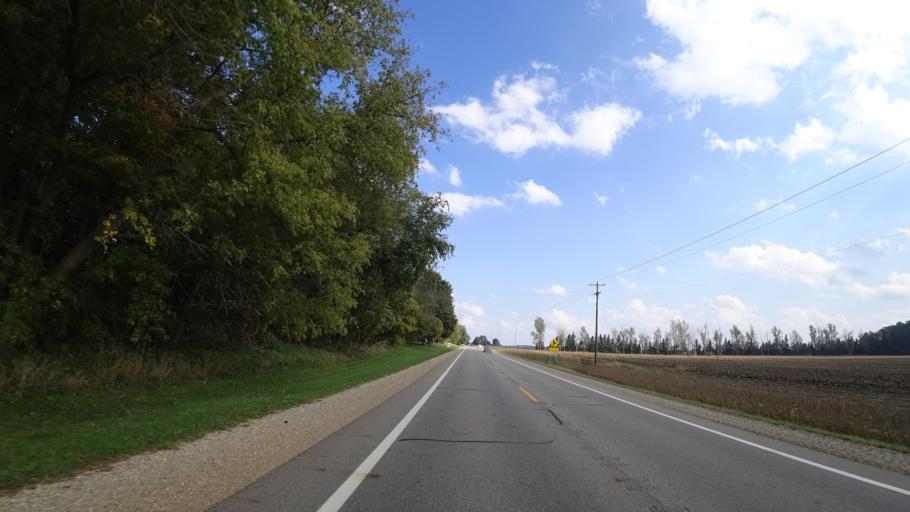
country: US
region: Michigan
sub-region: Saint Joseph County
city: Centreville
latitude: 42.0062
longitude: -85.5106
